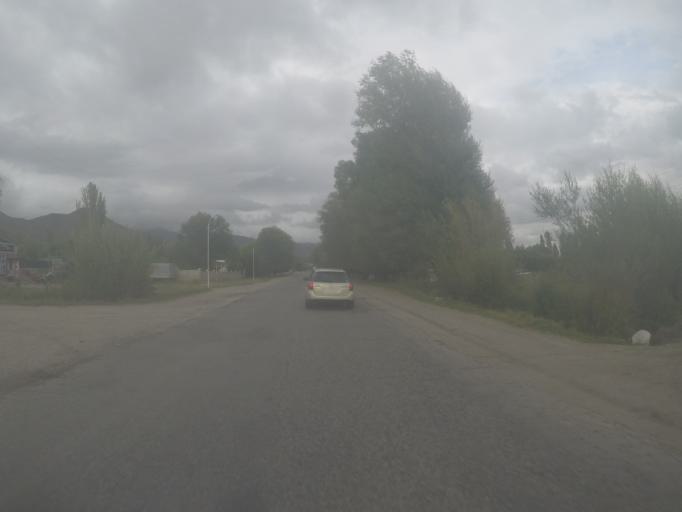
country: KG
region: Ysyk-Koel
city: Tyup
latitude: 42.7851
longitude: 78.2480
